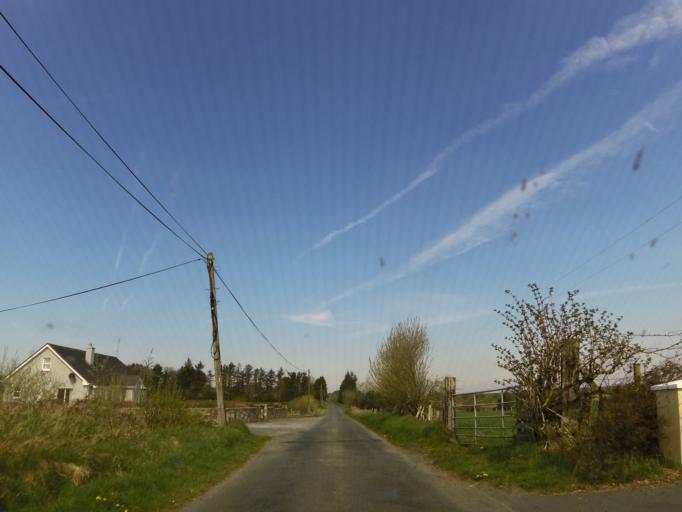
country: IE
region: Connaught
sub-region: Maigh Eo
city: Kiltamagh
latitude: 53.8089
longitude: -8.9760
